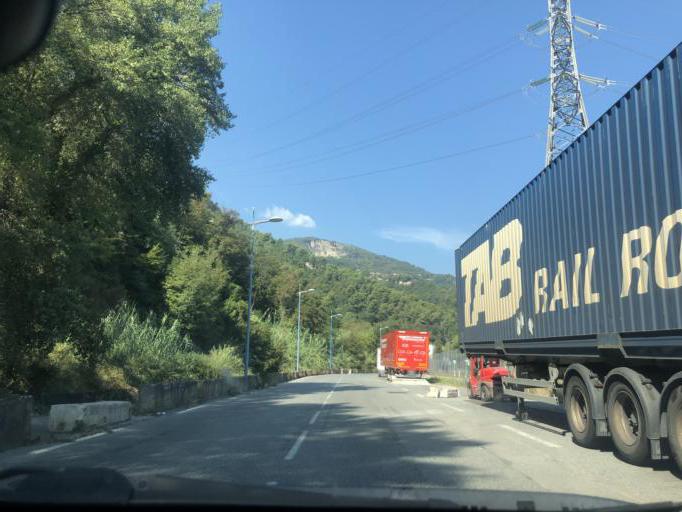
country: FR
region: Provence-Alpes-Cote d'Azur
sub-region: Departement des Alpes-Maritimes
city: Carros
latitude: 43.8021
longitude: 7.1911
